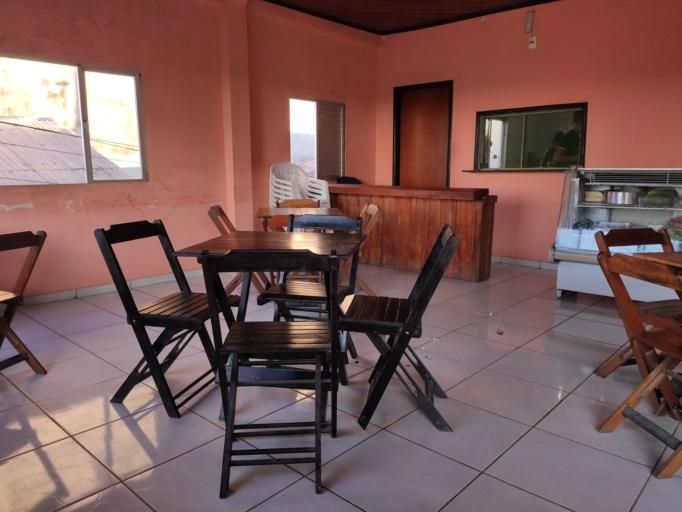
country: BR
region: Acre
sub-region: Marechal Thaumaturgo
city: Marechal Thaumaturgo
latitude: -8.9497
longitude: -72.7860
